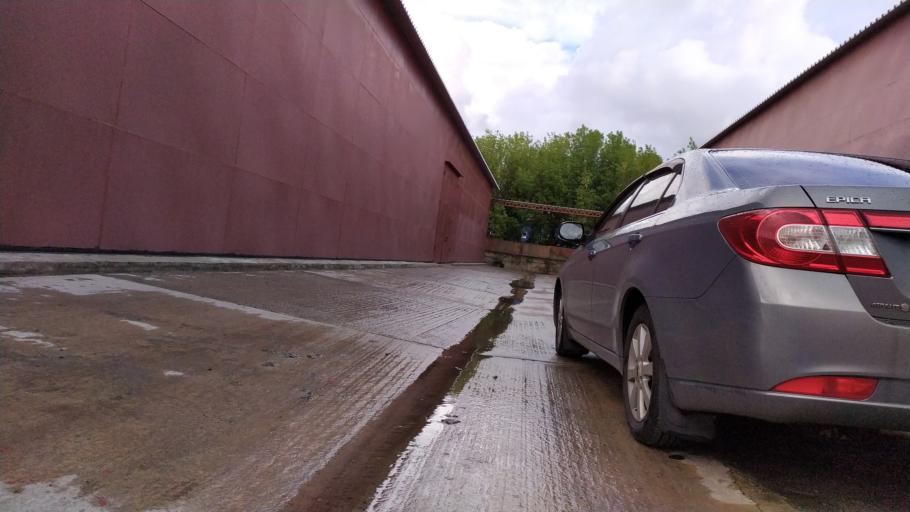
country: RU
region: Kursk
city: Kursk
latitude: 51.6999
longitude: 36.1751
